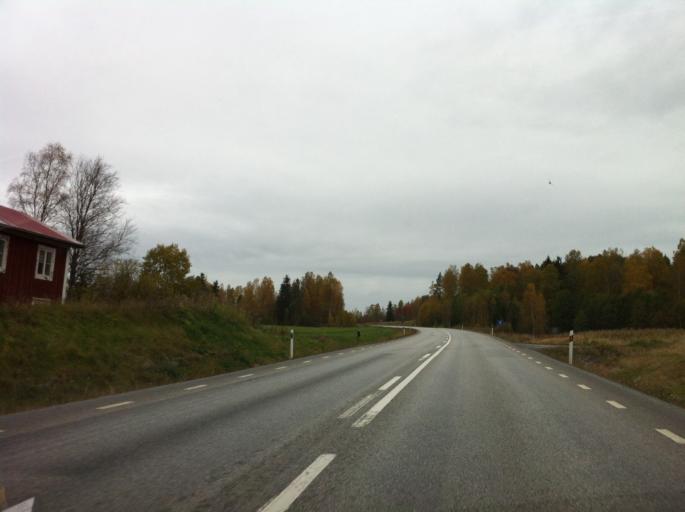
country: SE
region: OErebro
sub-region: Ljusnarsbergs Kommun
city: Kopparberg
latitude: 59.8357
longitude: 15.0982
